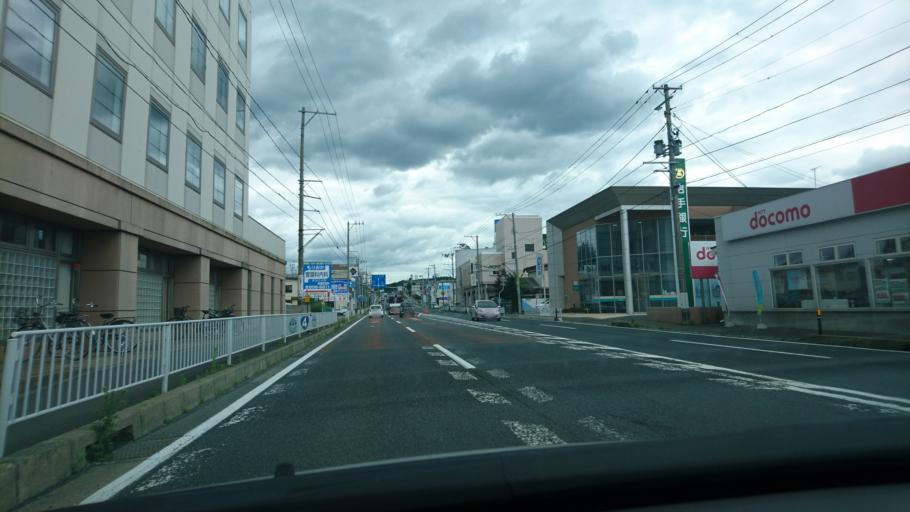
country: JP
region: Iwate
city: Morioka-shi
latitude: 39.6938
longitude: 141.1668
